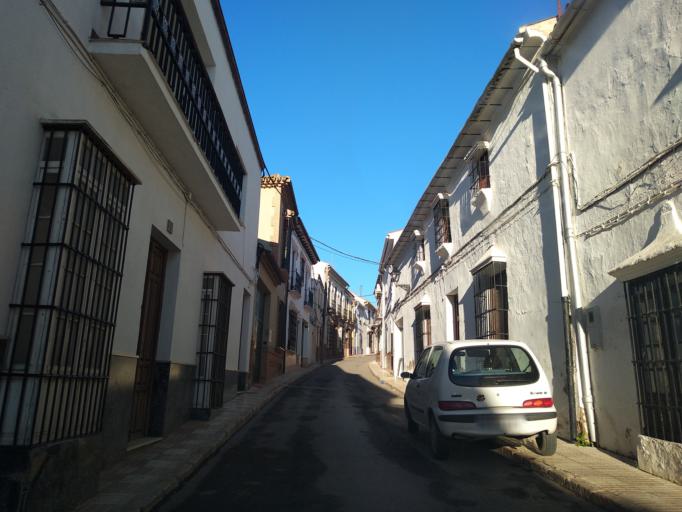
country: ES
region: Andalusia
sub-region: Provincia de Malaga
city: Campillos
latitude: 37.0487
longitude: -4.8634
